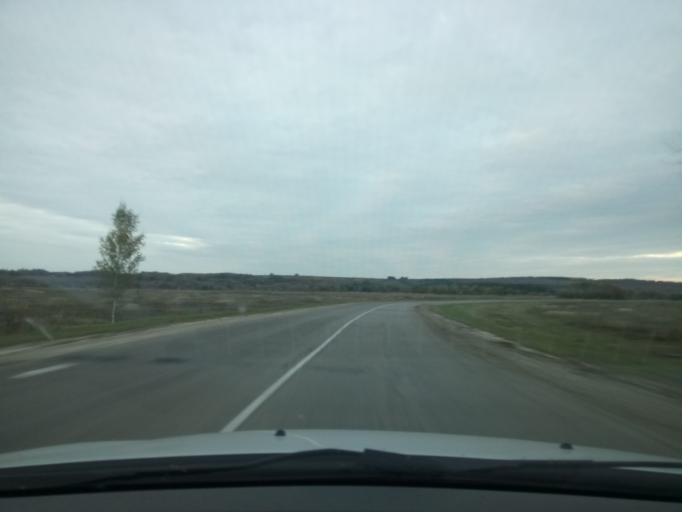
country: RU
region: Nizjnij Novgorod
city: Bol'shoye Murashkino
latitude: 55.7932
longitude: 44.7396
